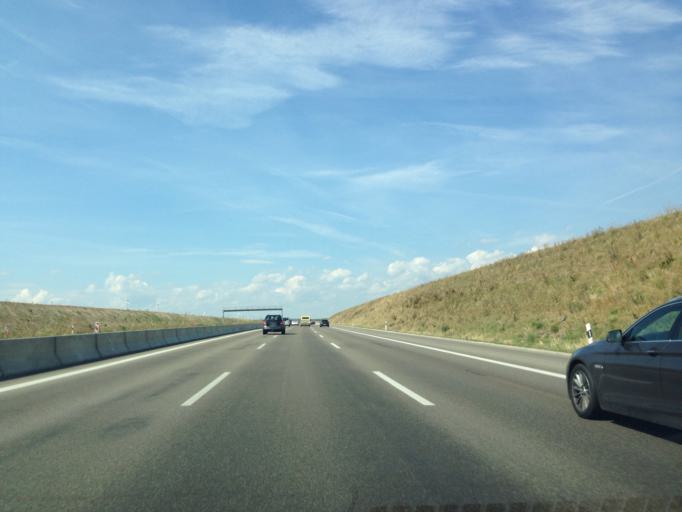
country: DE
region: Baden-Wuerttemberg
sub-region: Tuebingen Region
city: Dornstadt
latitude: 48.4641
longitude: 9.9213
